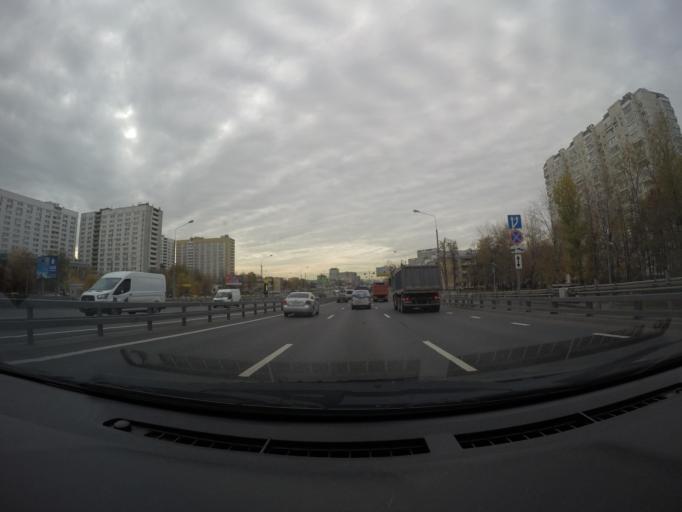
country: RU
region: Moscow
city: Yaroslavskiy
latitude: 55.8688
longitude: 37.7090
